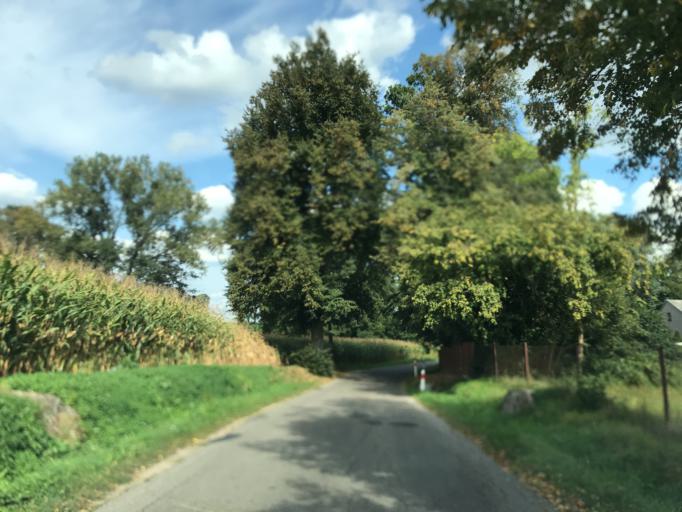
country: PL
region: Warmian-Masurian Voivodeship
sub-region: Powiat ilawski
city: Lubawa
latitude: 53.4111
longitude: 19.7527
